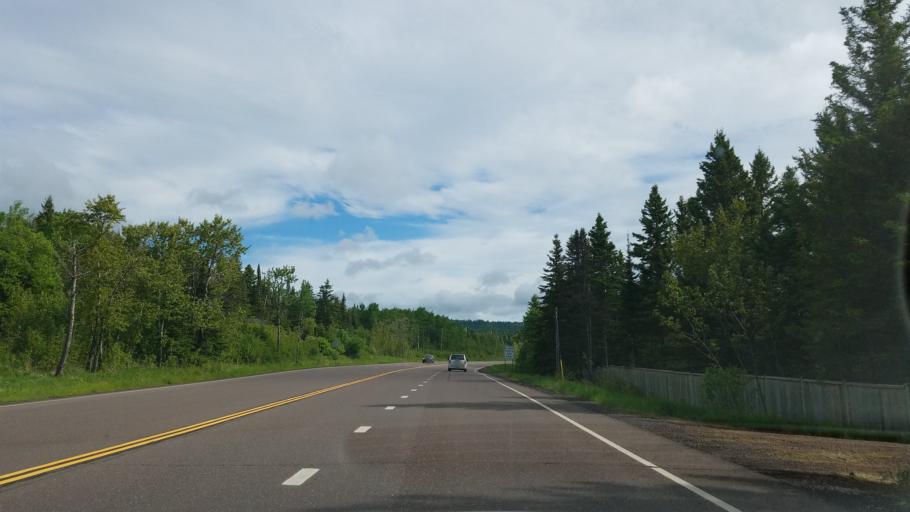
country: US
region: Minnesota
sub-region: Lake County
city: Two Harbors
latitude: 47.0791
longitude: -91.5854
